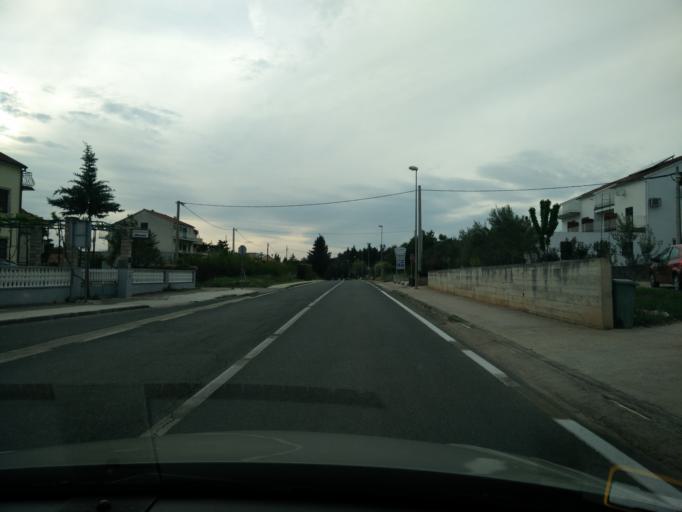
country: HR
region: Zadarska
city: Turanj
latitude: 43.9694
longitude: 15.4081
